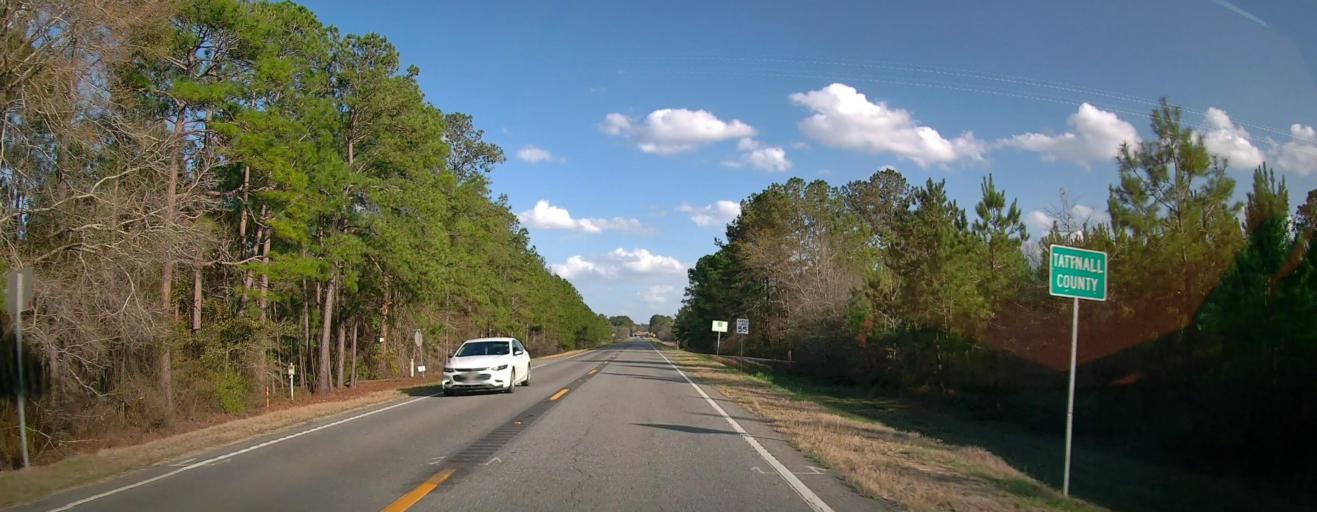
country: US
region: Georgia
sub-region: Tattnall County
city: Reidsville
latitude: 32.1210
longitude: -82.1970
